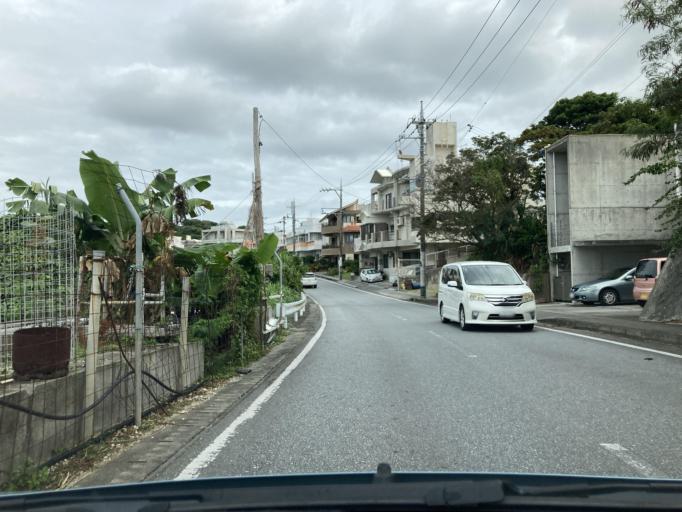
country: JP
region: Okinawa
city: Tomigusuku
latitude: 26.1611
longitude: 127.6787
